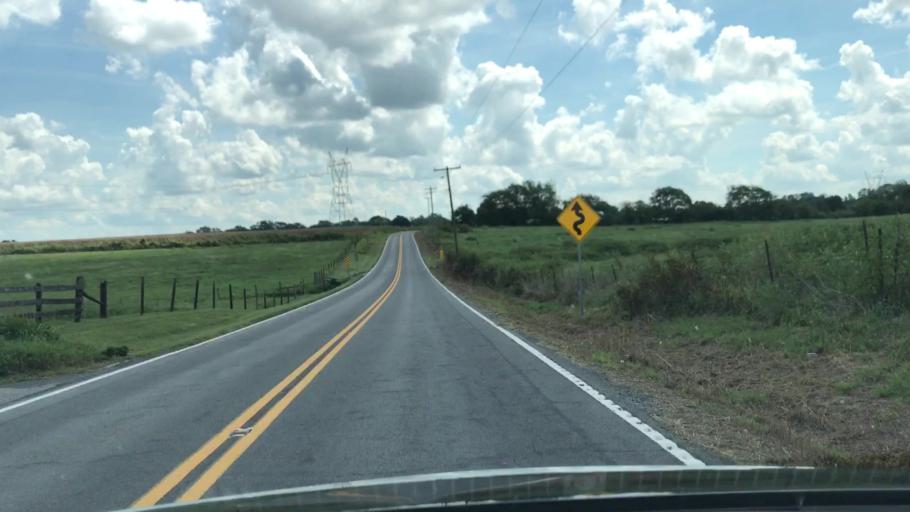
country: US
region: Tennessee
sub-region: Robertson County
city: Springfield
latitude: 36.5795
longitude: -86.8748
